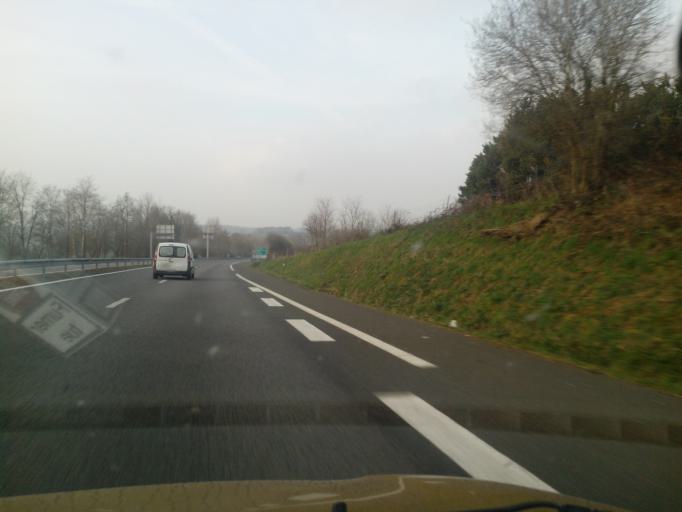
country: FR
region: Brittany
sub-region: Departement du Morbihan
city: Guillac
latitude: 47.8712
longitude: -2.4184
